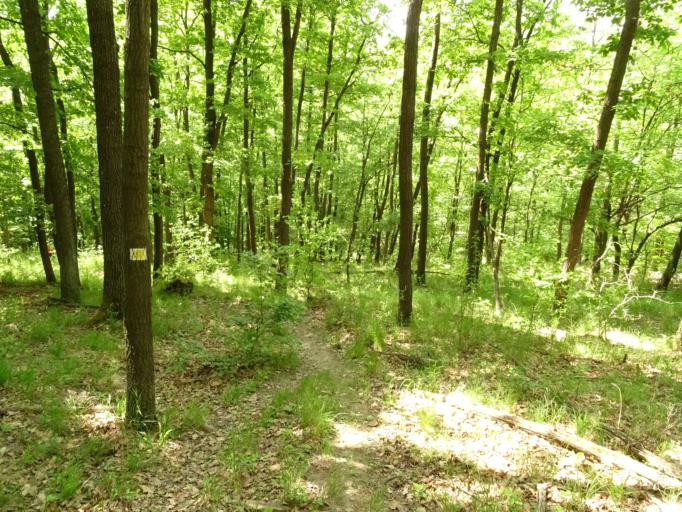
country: SK
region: Nitriansky
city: Sahy
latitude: 47.9961
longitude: 18.9512
